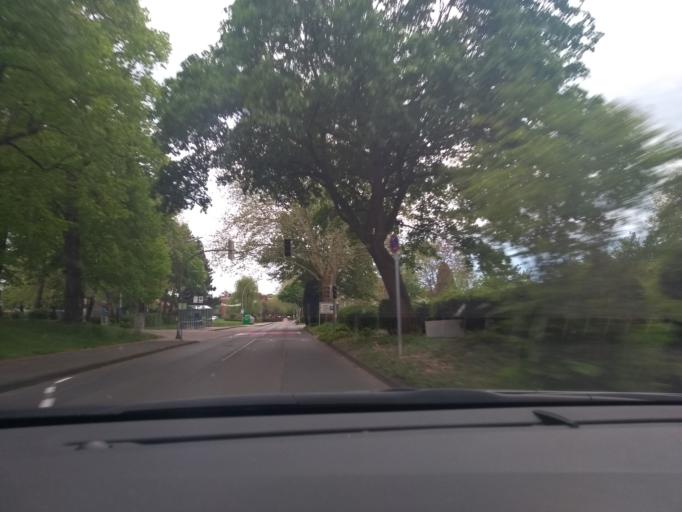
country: DE
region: North Rhine-Westphalia
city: Selm
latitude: 51.6637
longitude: 7.4670
